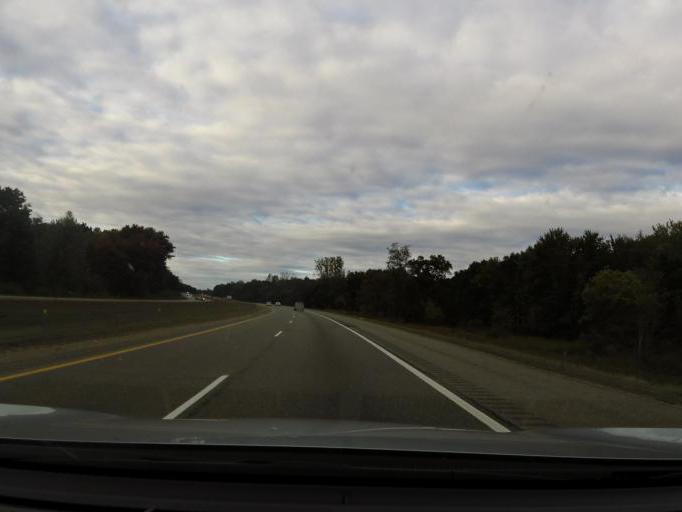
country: US
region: Michigan
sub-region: Livingston County
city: Brighton
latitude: 42.5612
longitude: -83.7402
